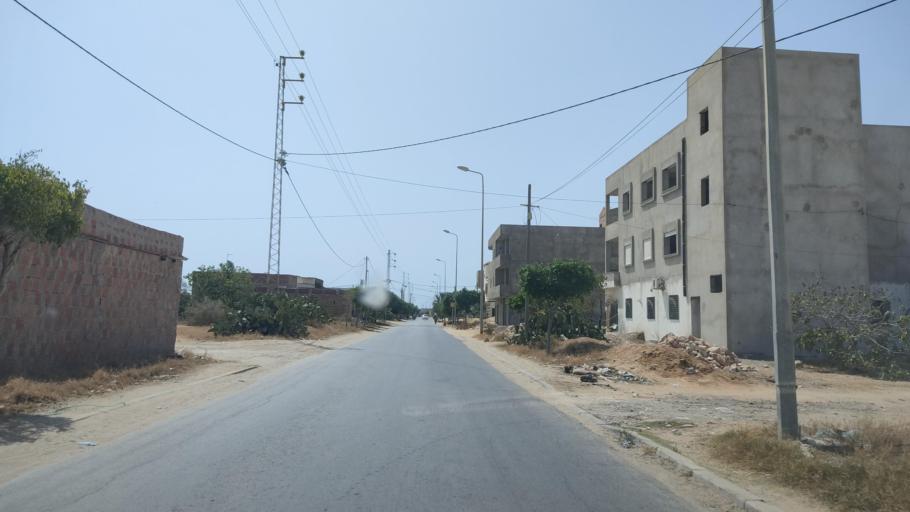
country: TN
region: Safaqis
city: Sfax
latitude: 34.6726
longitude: 10.7031
